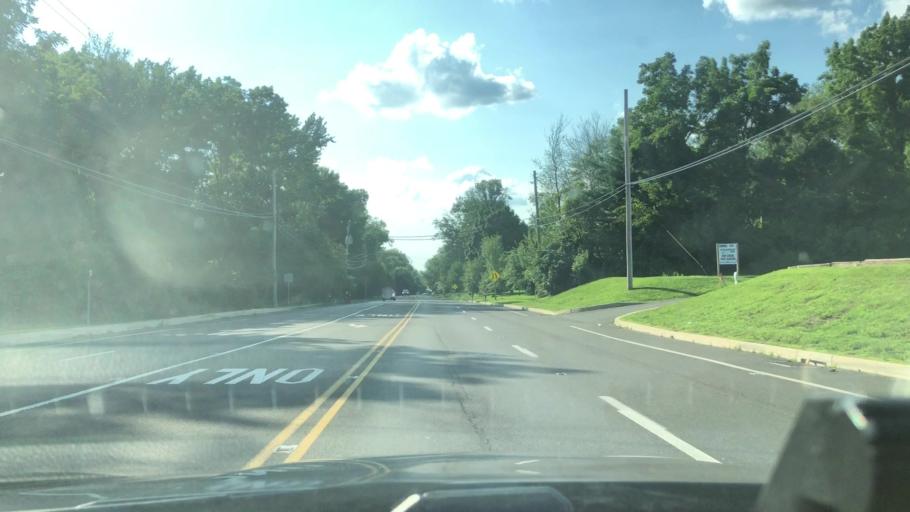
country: US
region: Pennsylvania
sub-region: Bucks County
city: Brittany Farms-Highlands
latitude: 40.2667
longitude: -75.2298
